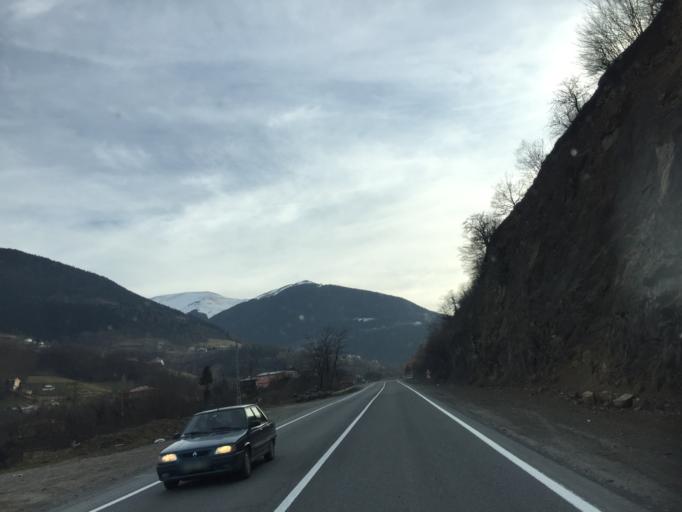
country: TR
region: Trabzon
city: Macka
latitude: 40.7220
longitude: 39.5188
